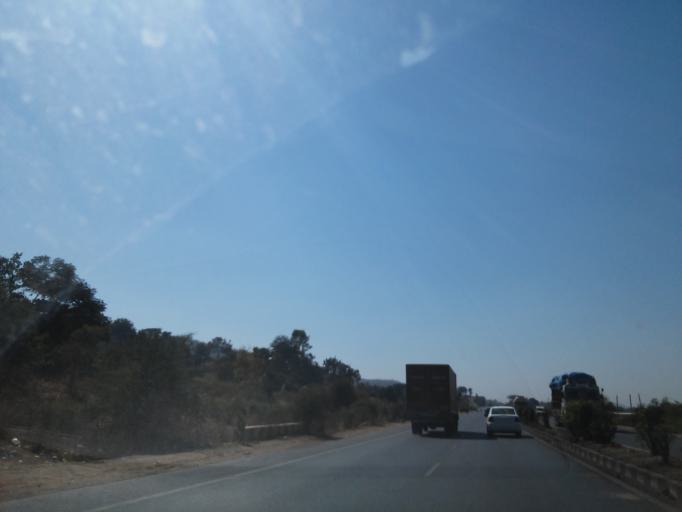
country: IN
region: Gujarat
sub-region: Sabar Kantha
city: Meghraj
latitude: 23.7530
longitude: 73.4396
